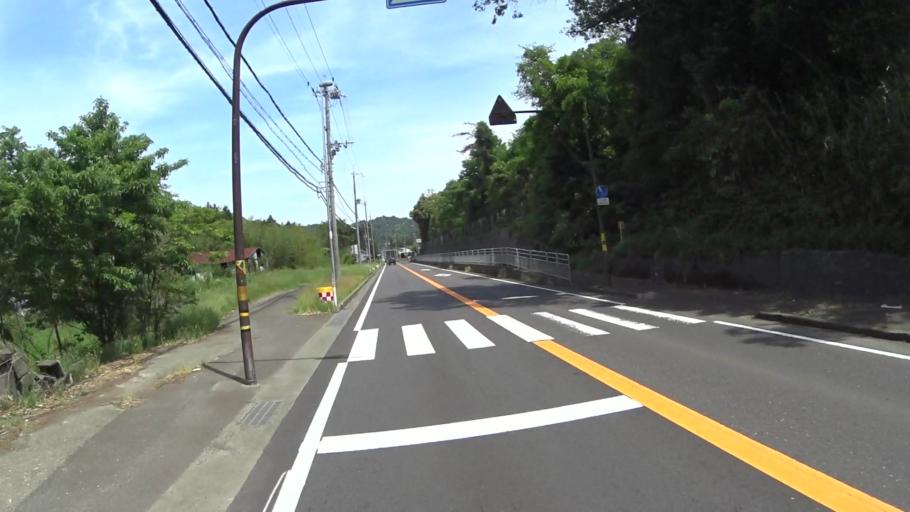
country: JP
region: Fukui
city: Obama
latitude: 35.4817
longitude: 135.6727
